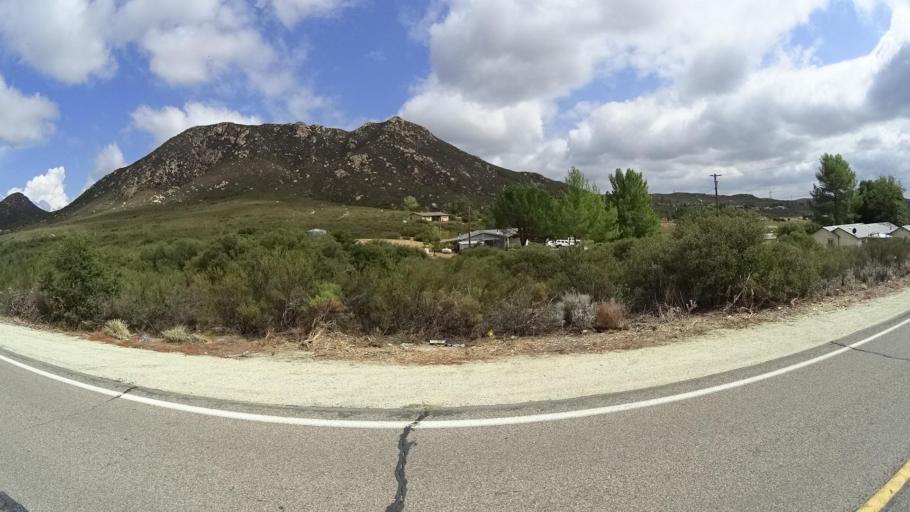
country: US
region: California
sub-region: San Diego County
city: Campo
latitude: 32.6796
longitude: -116.4888
